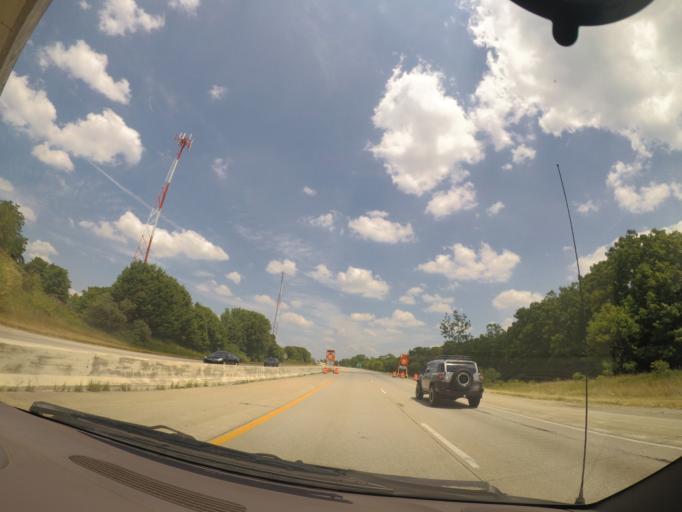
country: US
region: Indiana
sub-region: Saint Joseph County
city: Osceola
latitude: 41.6192
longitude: -86.0411
